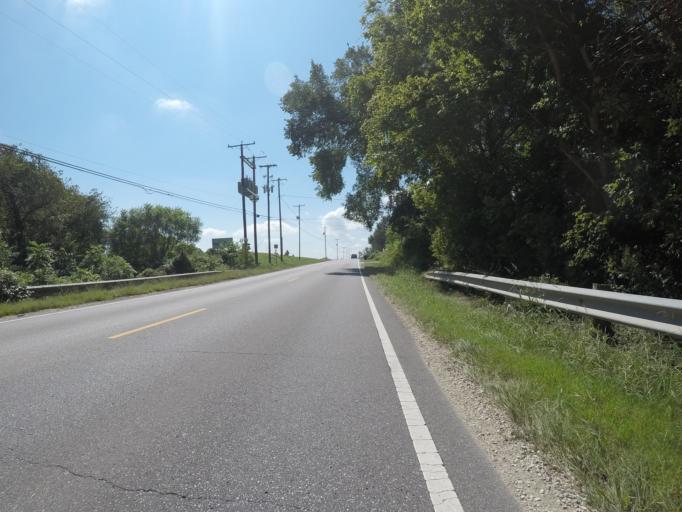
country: US
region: Ohio
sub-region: Lawrence County
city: South Point
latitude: 38.4445
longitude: -82.5942
